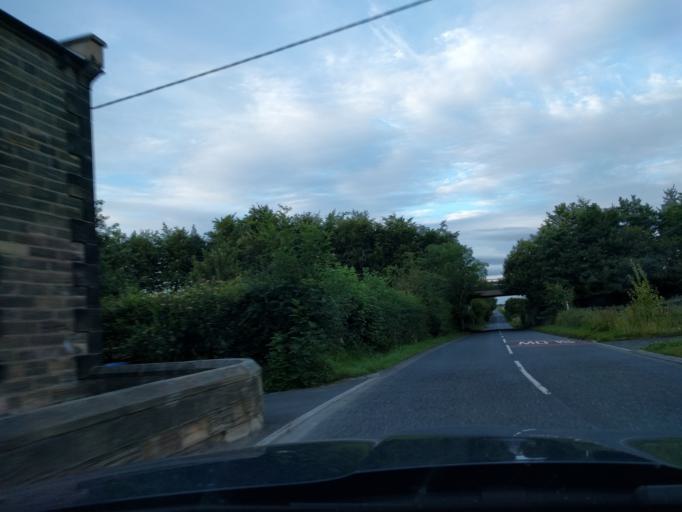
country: GB
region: England
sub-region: Northumberland
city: Stannington
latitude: 55.0833
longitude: -1.6493
